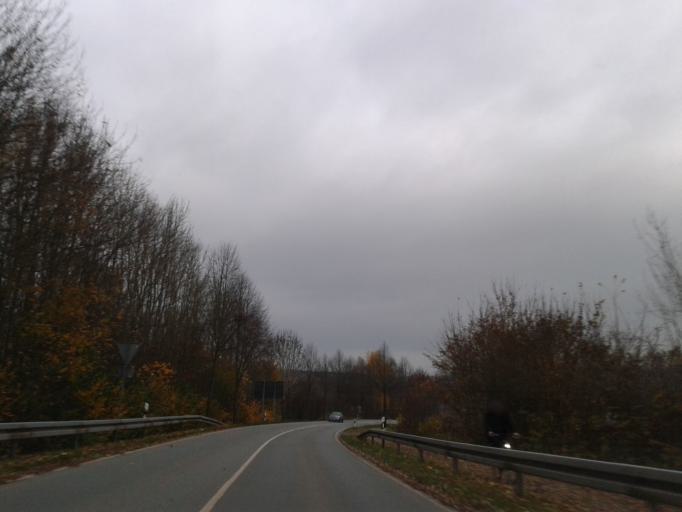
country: DE
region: North Rhine-Westphalia
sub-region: Regierungsbezirk Detmold
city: Blomberg
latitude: 51.9150
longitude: 9.1444
